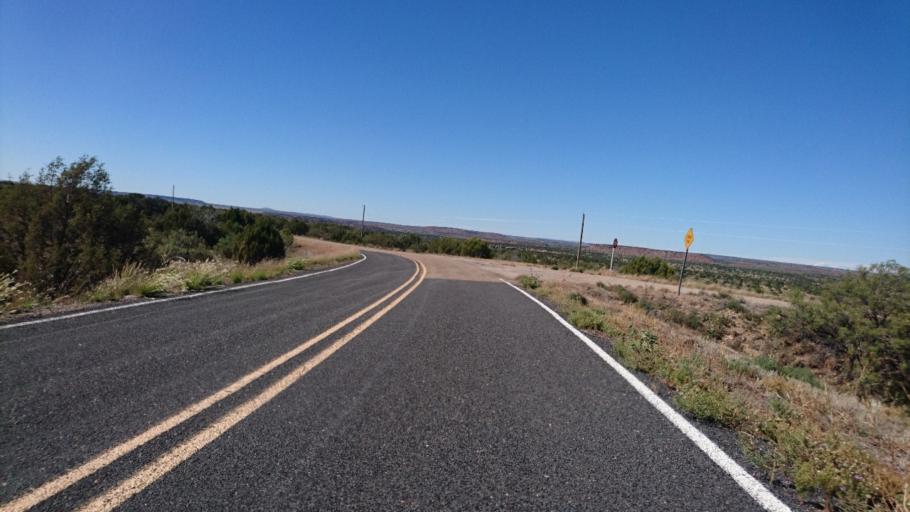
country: US
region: New Mexico
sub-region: Quay County
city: Tucumcari
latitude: 35.0672
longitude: -104.1801
